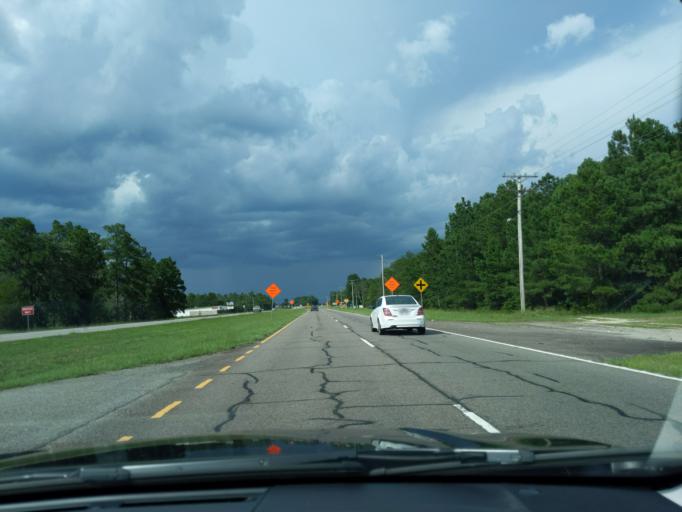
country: US
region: South Carolina
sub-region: Edgefield County
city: Murphys Estates
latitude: 33.6441
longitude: -81.9052
